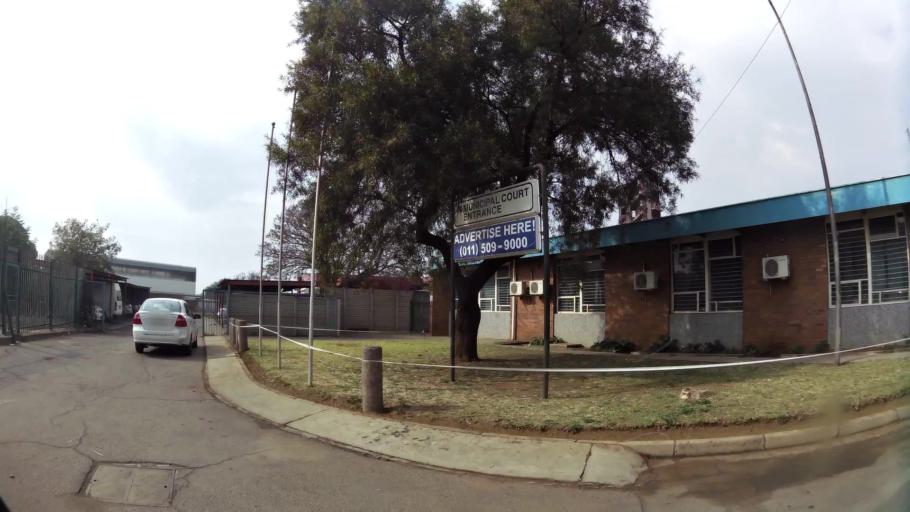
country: ZA
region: Gauteng
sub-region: Sedibeng District Municipality
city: Vanderbijlpark
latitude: -26.6823
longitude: 27.8354
